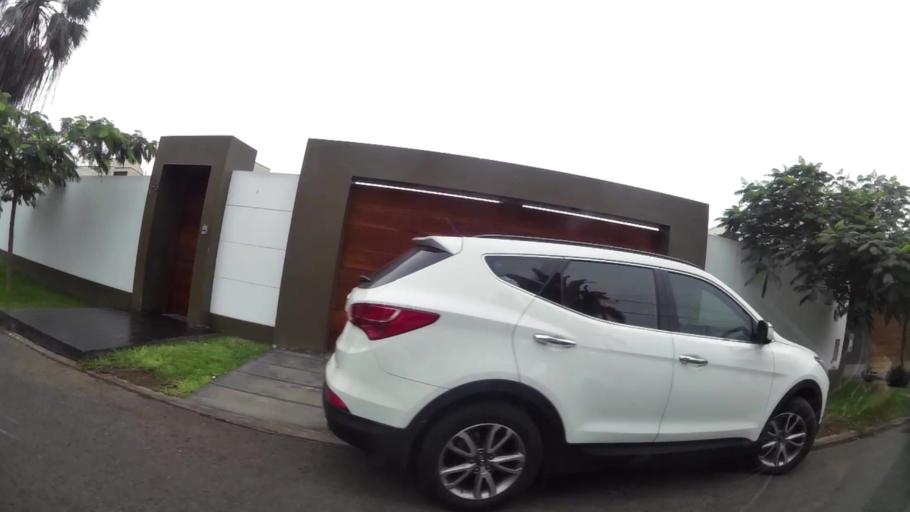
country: PE
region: Lima
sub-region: Lima
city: La Molina
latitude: -12.0902
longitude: -76.9243
